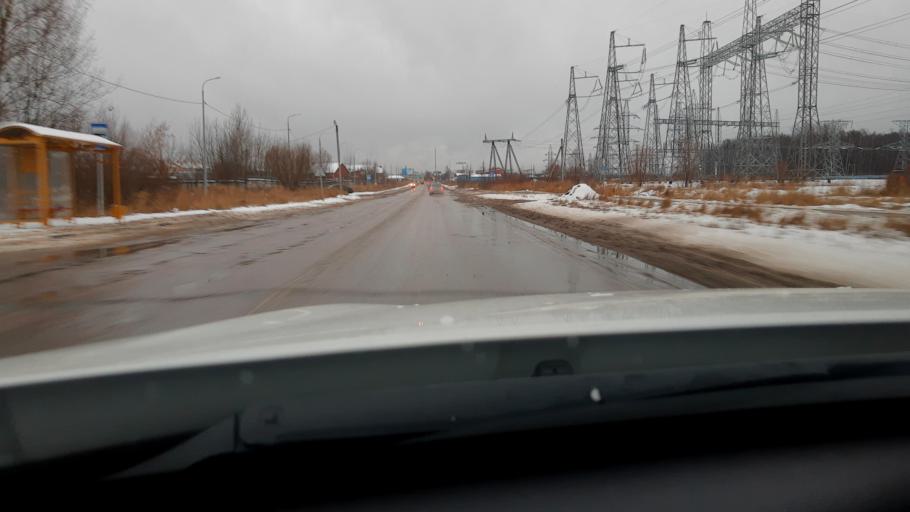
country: RU
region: Moskovskaya
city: Krasnogorsk
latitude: 55.8592
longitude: 37.3340
